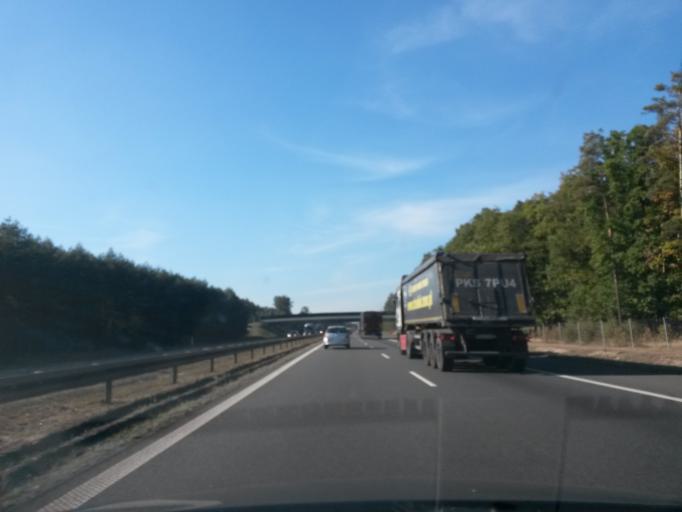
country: PL
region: Opole Voivodeship
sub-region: Powiat opolski
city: Komprachcice
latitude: 50.5918
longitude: 17.8076
